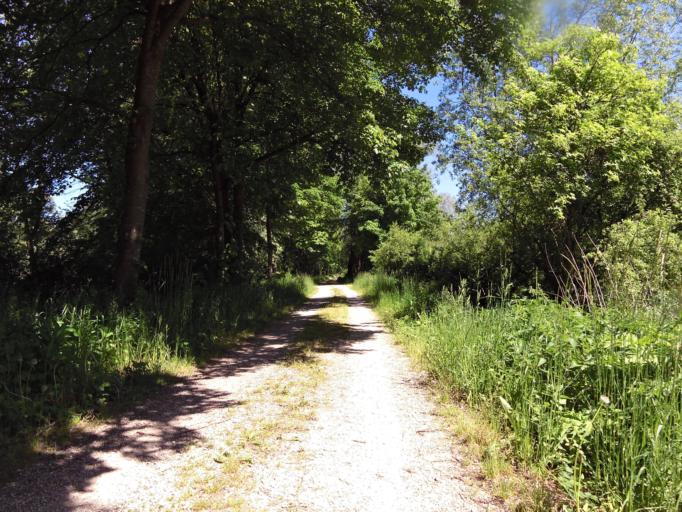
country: DE
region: Bavaria
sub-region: Upper Bavaria
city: Langenbach
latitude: 48.4182
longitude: 11.8654
